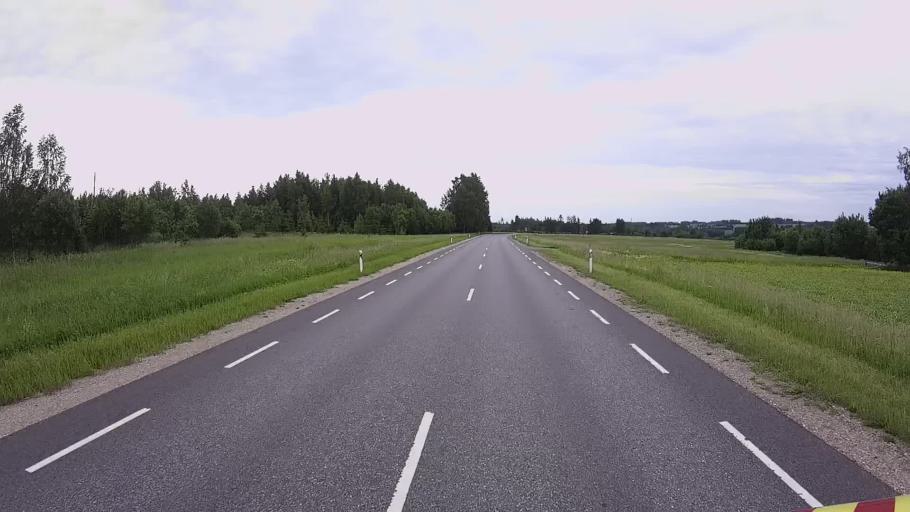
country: EE
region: Viljandimaa
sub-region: Karksi vald
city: Karksi-Nuia
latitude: 58.1555
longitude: 25.5953
